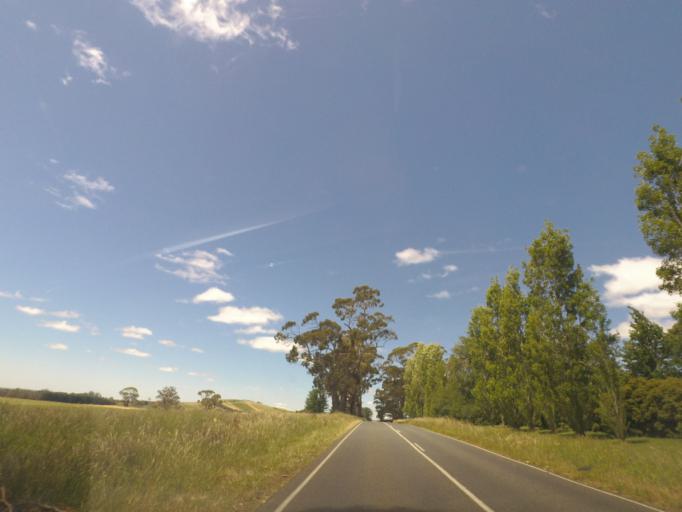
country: AU
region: Victoria
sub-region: Mount Alexander
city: Castlemaine
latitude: -37.3219
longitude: 144.1998
